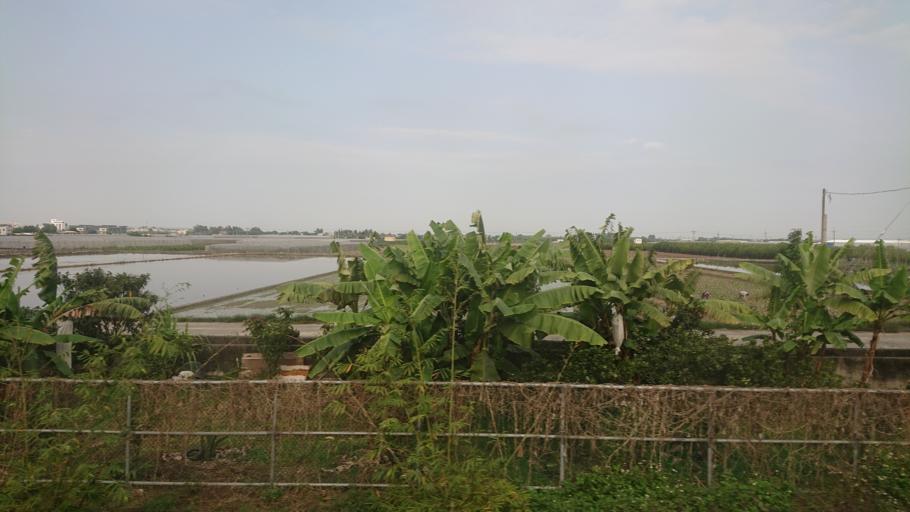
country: TW
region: Taiwan
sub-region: Yunlin
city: Douliu
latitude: 23.7308
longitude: 120.5788
